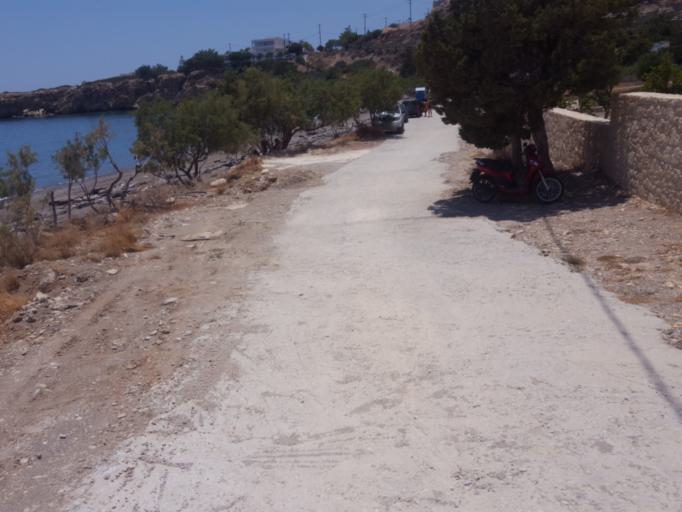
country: GR
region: Crete
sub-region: Nomos Lasithiou
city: Kato Chorio
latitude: 35.0153
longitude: 25.8433
